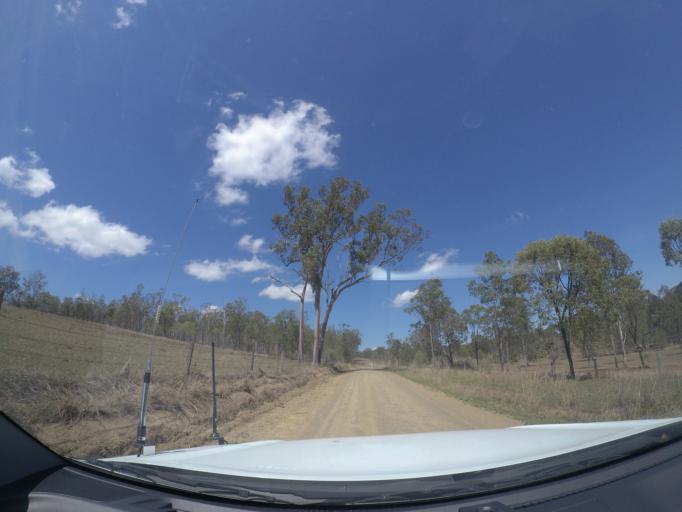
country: AU
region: Queensland
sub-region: Logan
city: Cedar Vale
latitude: -27.8552
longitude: 152.8850
